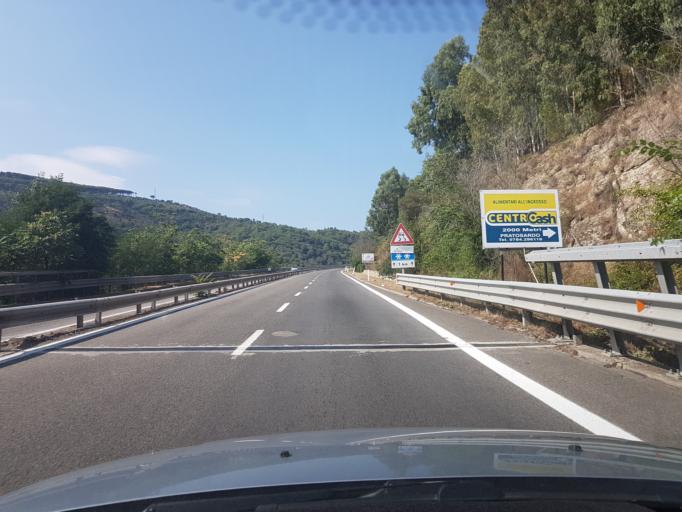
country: IT
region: Sardinia
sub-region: Provincia di Nuoro
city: Nuoro
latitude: 40.3369
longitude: 9.3001
